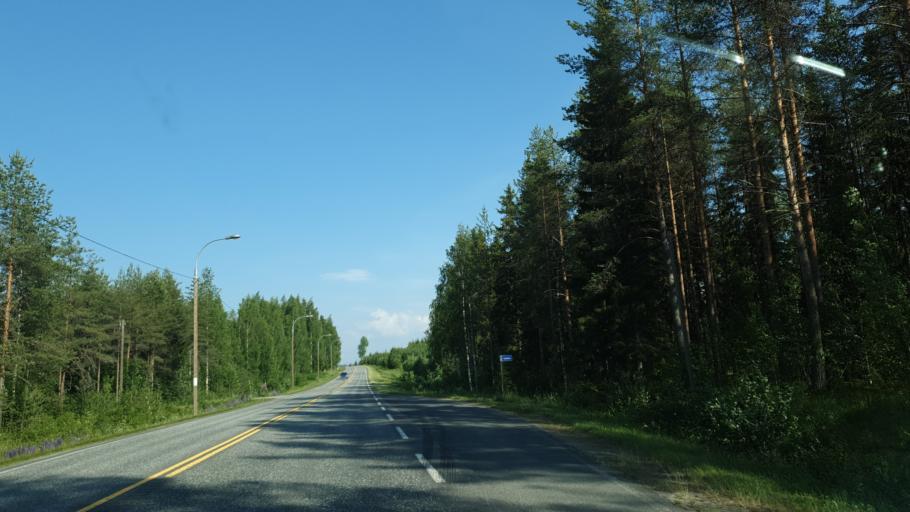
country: FI
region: Northern Savo
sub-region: Kuopio
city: Nilsiae
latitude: 63.1440
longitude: 27.8903
